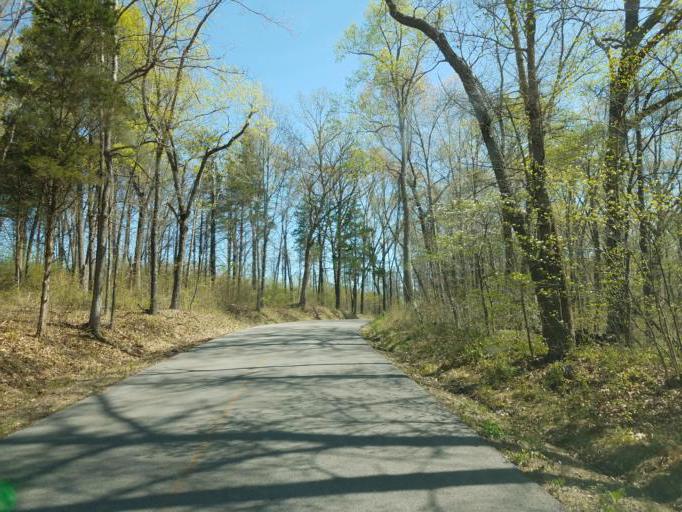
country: US
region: Kentucky
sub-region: Barren County
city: Cave City
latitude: 37.1957
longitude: -86.0863
